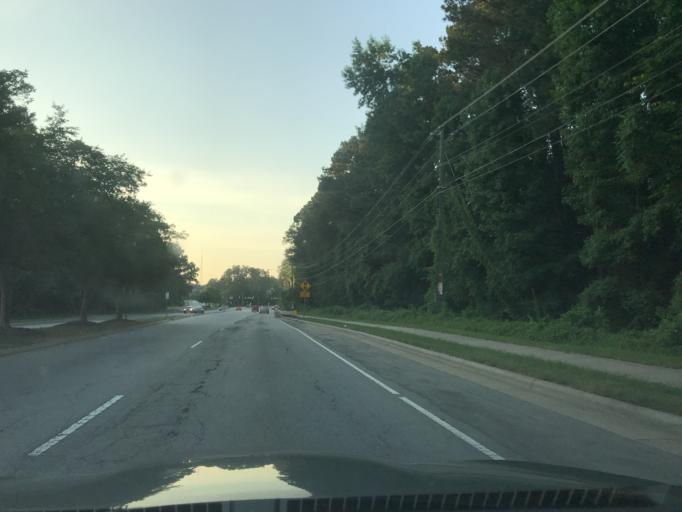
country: US
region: North Carolina
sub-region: Wake County
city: Raleigh
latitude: 35.7626
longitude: -78.6142
